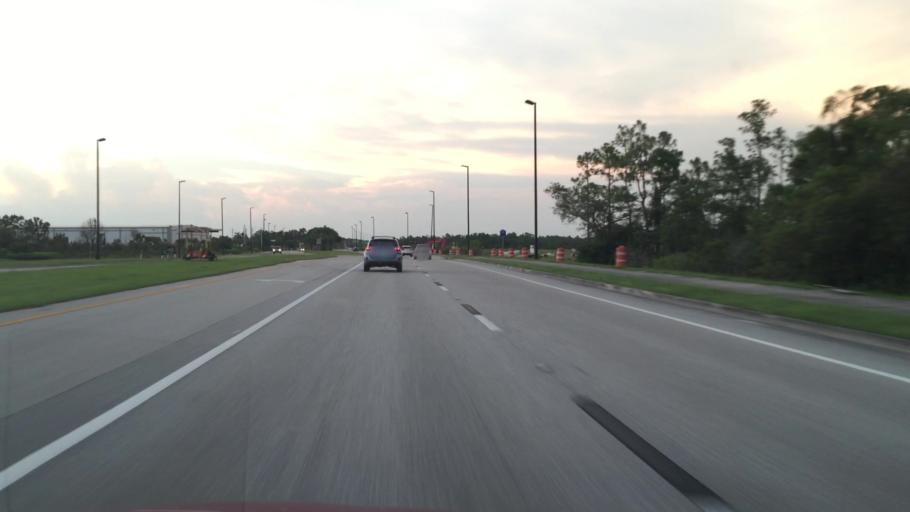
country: US
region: Florida
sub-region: Lee County
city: Gateway
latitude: 26.5356
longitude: -81.7857
